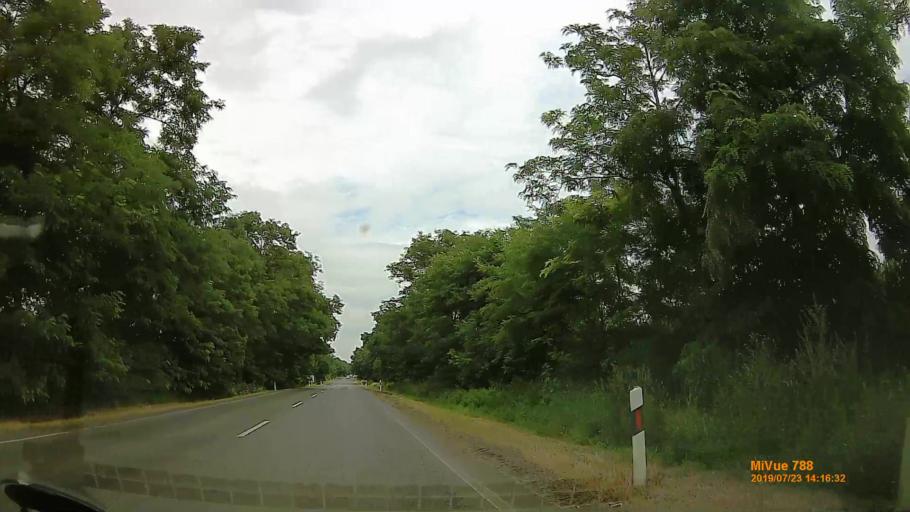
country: HU
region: Szabolcs-Szatmar-Bereg
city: Nagycserkesz
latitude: 47.9610
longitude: 21.5353
